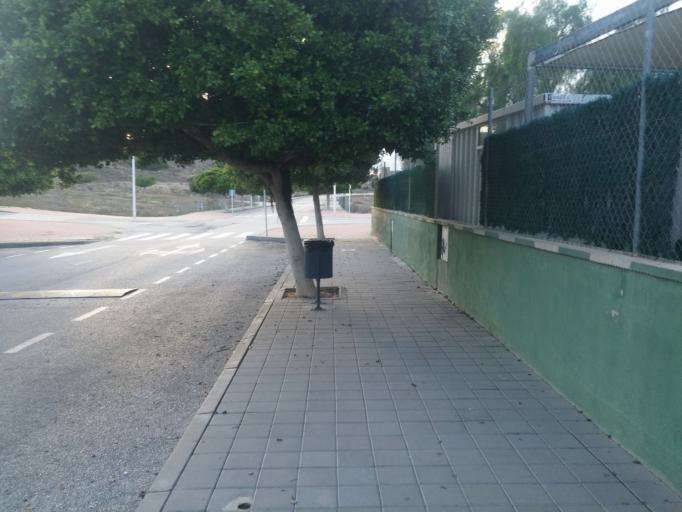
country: ES
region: Valencia
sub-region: Provincia de Alicante
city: Villajoyosa
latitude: 38.5011
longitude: -0.2418
